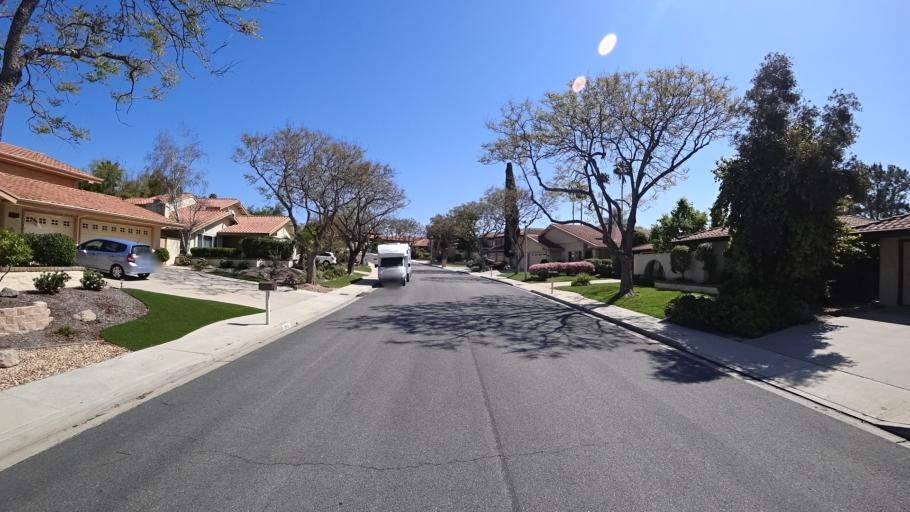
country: US
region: California
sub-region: Ventura County
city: Thousand Oaks
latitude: 34.2320
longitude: -118.8482
